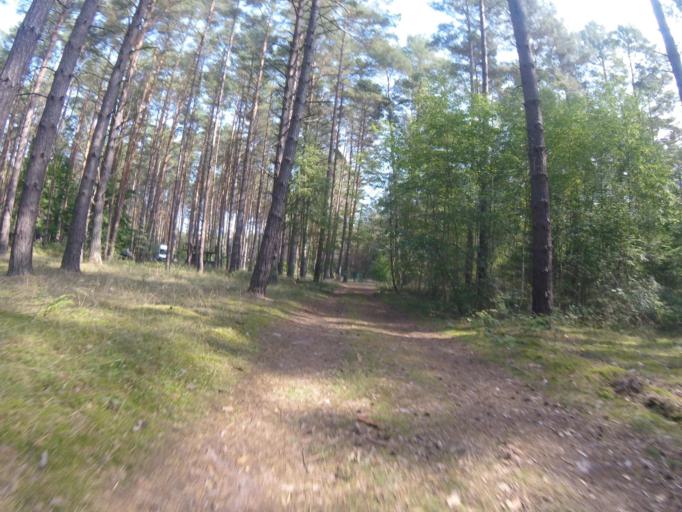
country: DE
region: Brandenburg
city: Bestensee
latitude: 52.2553
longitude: 13.6886
